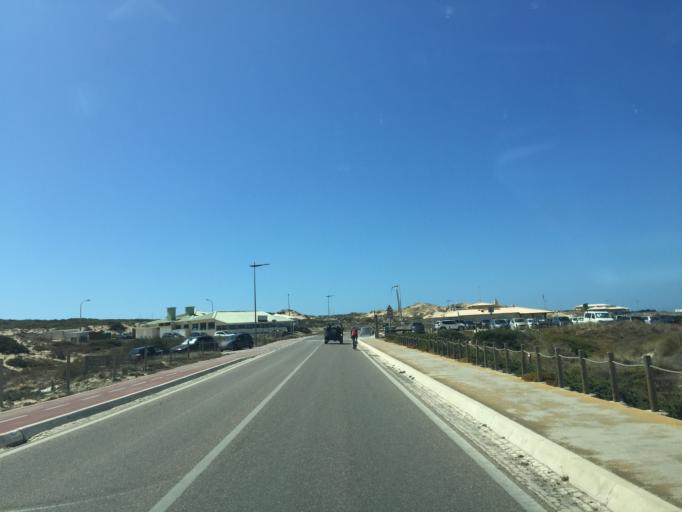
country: PT
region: Lisbon
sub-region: Cascais
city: Cascais
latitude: 38.7258
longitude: -9.4744
